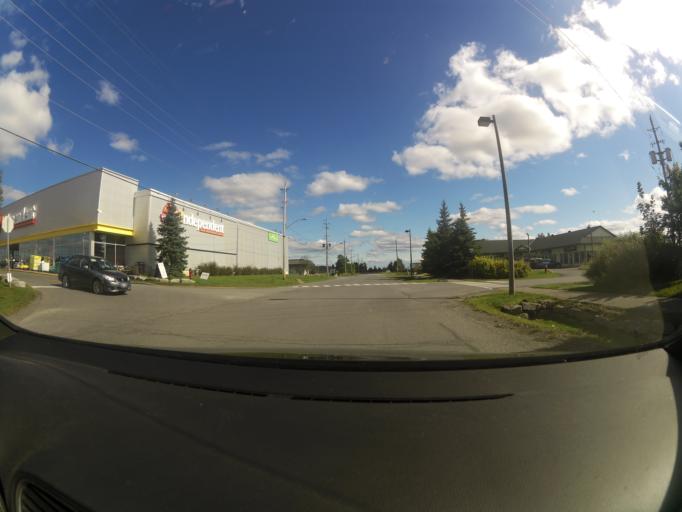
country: CA
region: Ontario
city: Carleton Place
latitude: 45.2339
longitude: -76.1832
